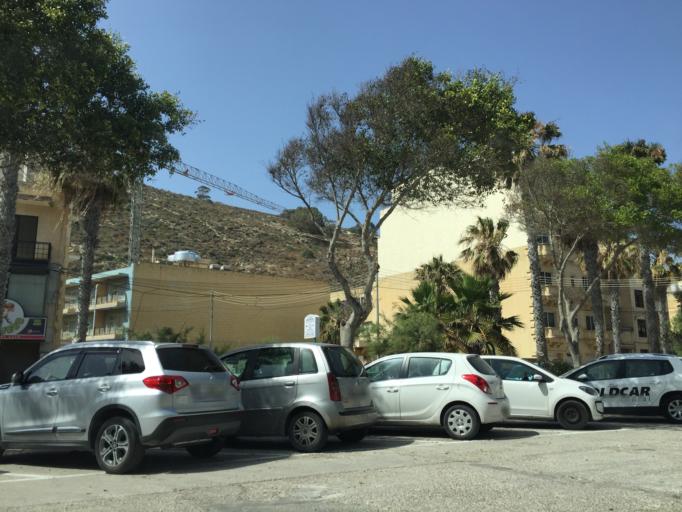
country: MT
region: Saint Lucia
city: Saint Lucia
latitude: 36.0306
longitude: 14.2182
